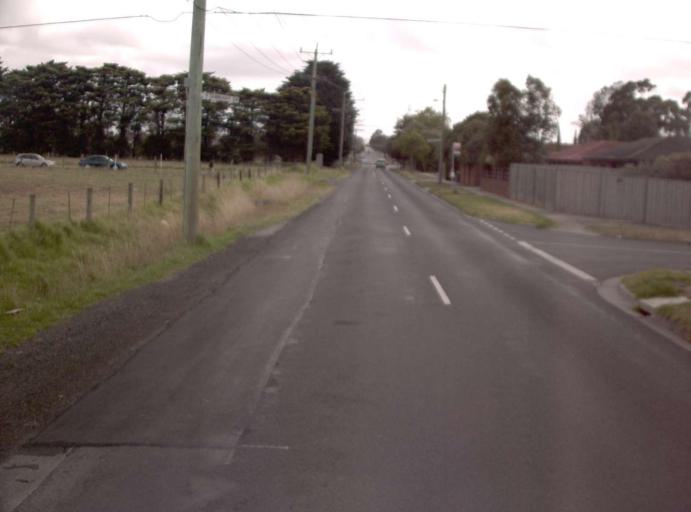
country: AU
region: Victoria
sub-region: Monash
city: Oakleigh South
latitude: -37.9431
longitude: 145.0974
